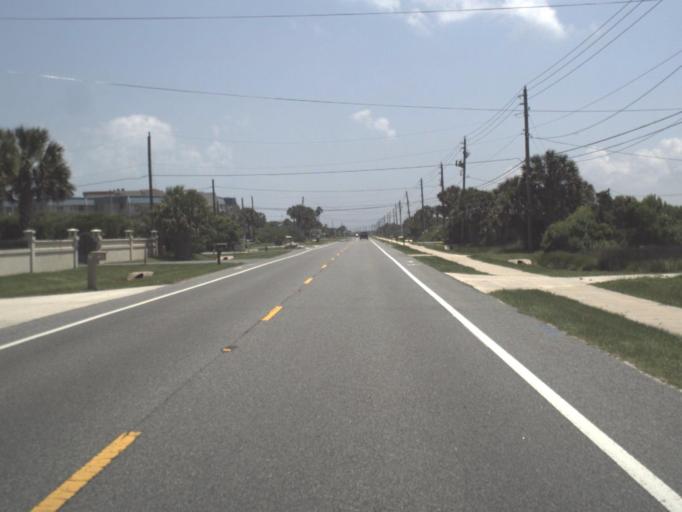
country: US
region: Florida
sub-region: Saint Johns County
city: Butler Beach
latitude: 29.7472
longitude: -81.2454
